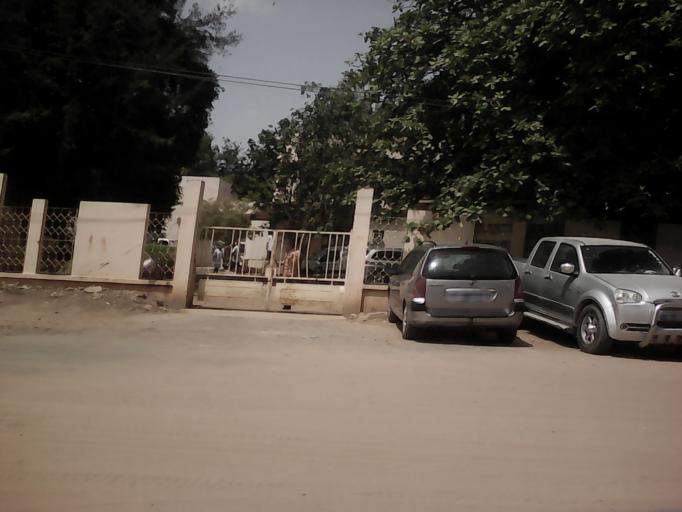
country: SN
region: Dakar
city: Grand Dakar
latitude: 14.7309
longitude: -17.4307
